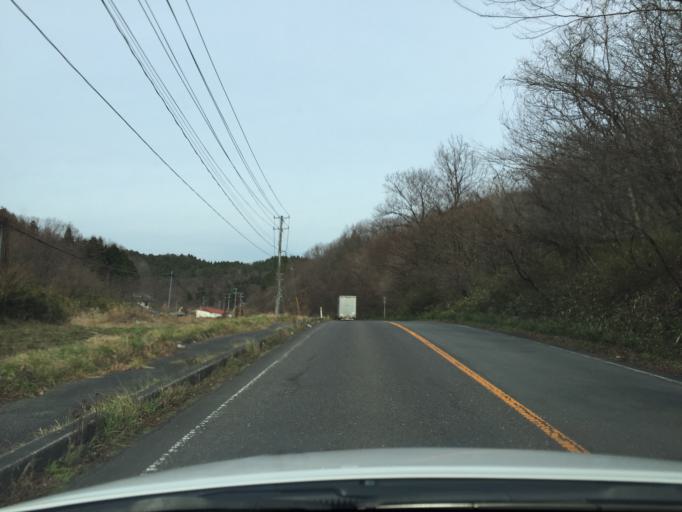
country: JP
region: Fukushima
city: Funehikimachi-funehiki
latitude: 37.2545
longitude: 140.6383
